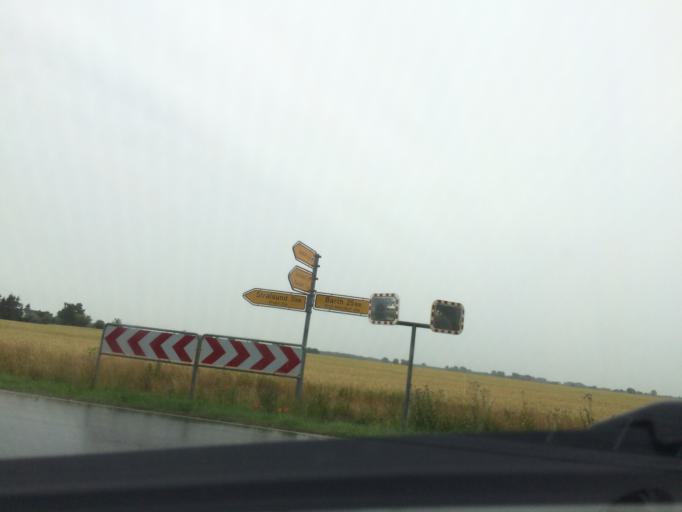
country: DE
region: Mecklenburg-Vorpommern
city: Prohn
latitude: 54.3852
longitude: 13.0019
